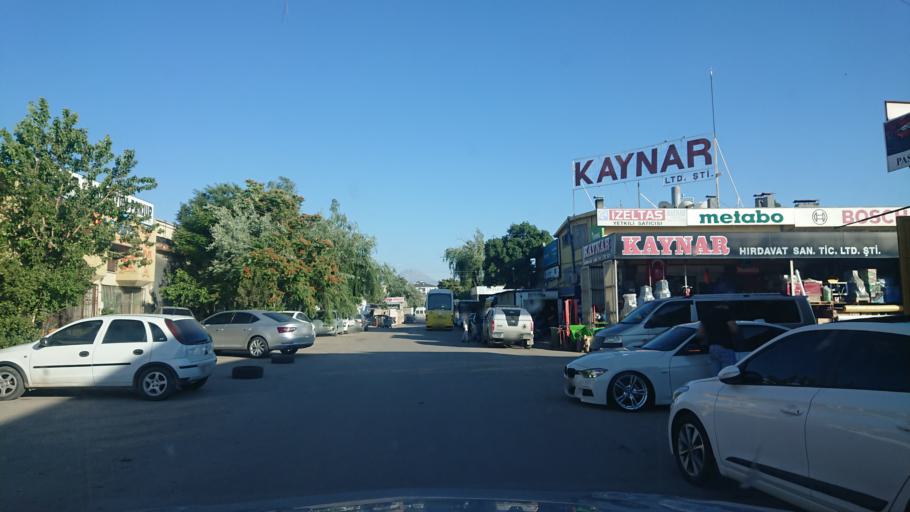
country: TR
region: Aksaray
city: Aksaray
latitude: 38.3729
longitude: 33.9962
